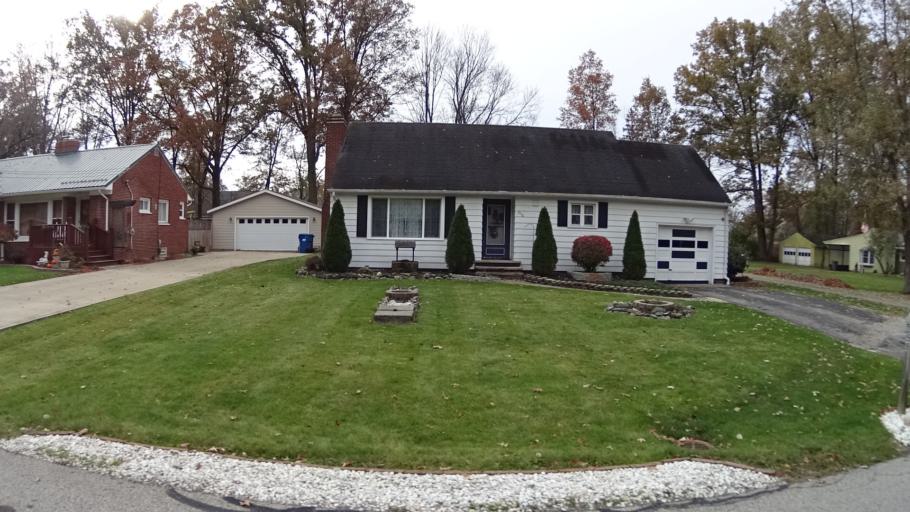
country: US
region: Ohio
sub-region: Lorain County
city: Elyria
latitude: 41.3417
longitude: -82.0988
